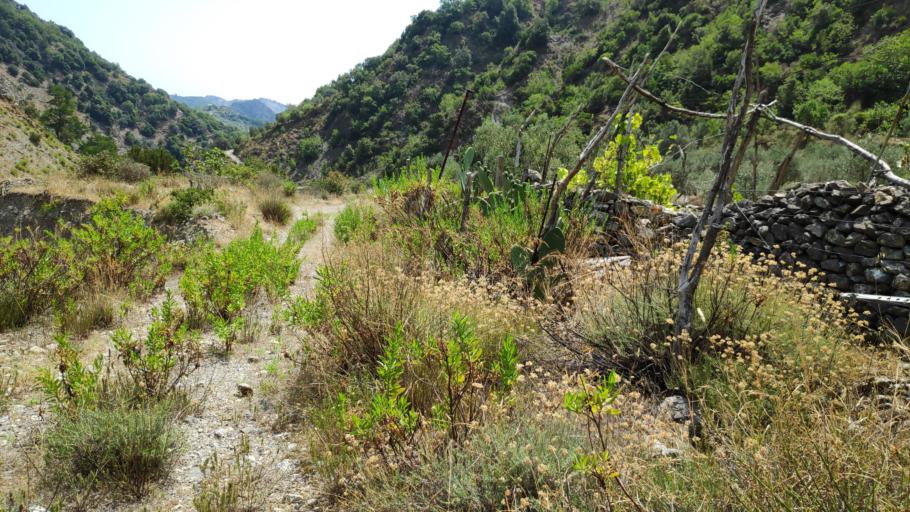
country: IT
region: Calabria
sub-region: Provincia di Reggio Calabria
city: Bivongi
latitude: 38.4936
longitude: 16.4487
